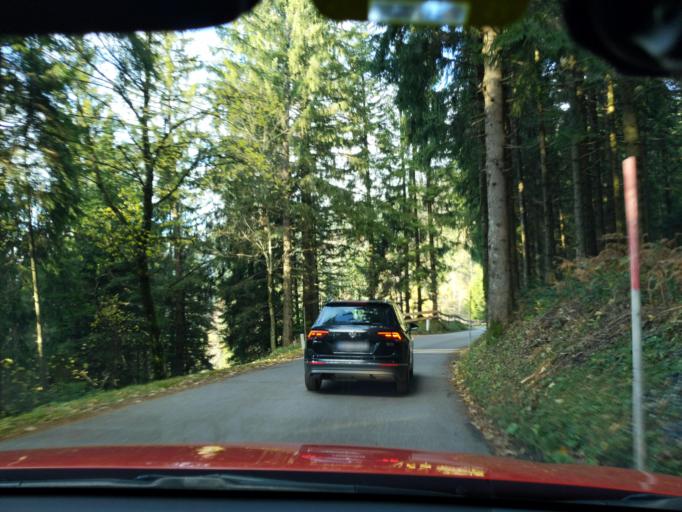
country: AT
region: Vorarlberg
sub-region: Politischer Bezirk Bregenz
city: Eichenberg
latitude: 47.5143
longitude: 9.7810
